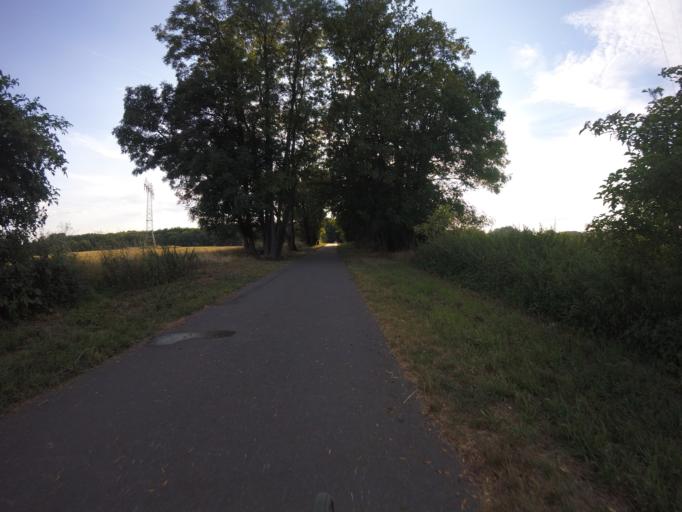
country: DE
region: Brandenburg
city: Neuenhagen
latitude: 52.5771
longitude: 13.6812
